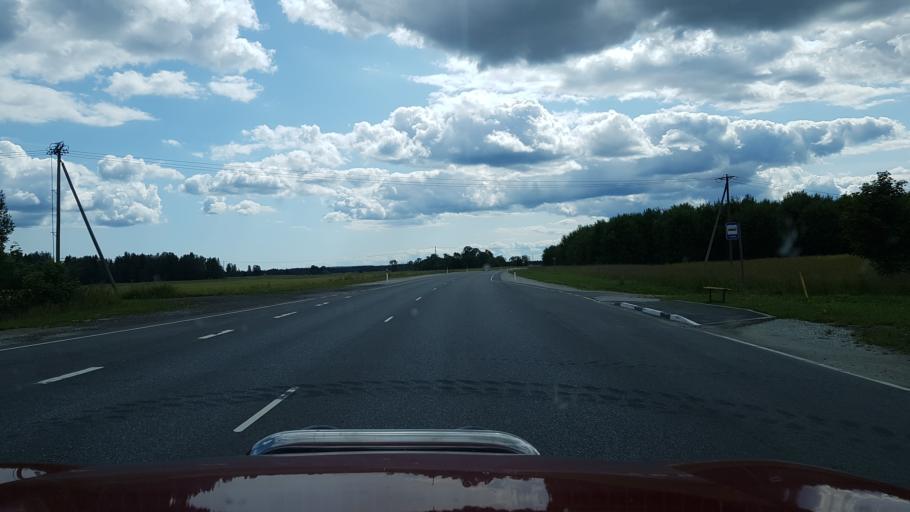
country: EE
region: Ida-Virumaa
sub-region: Johvi vald
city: Johvi
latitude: 59.2569
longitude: 27.3831
